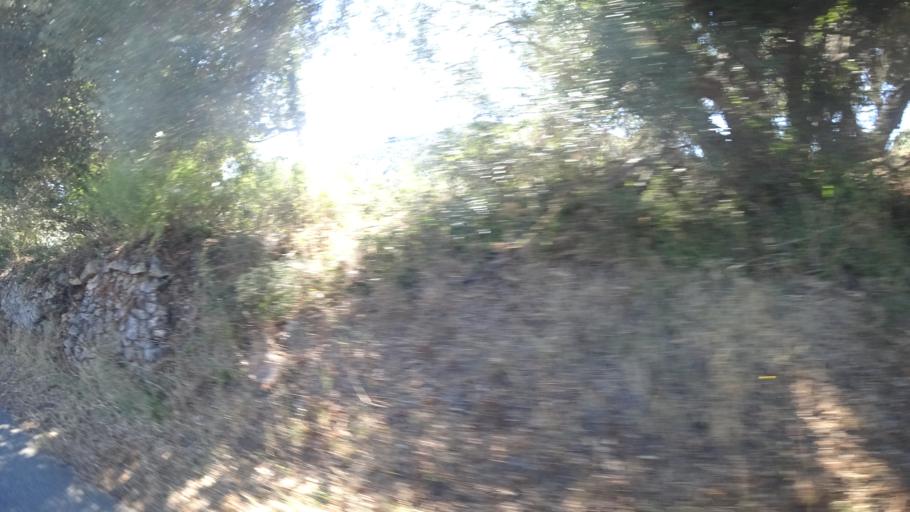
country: FR
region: Corsica
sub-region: Departement de la Corse-du-Sud
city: Alata
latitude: 41.9660
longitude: 8.7191
